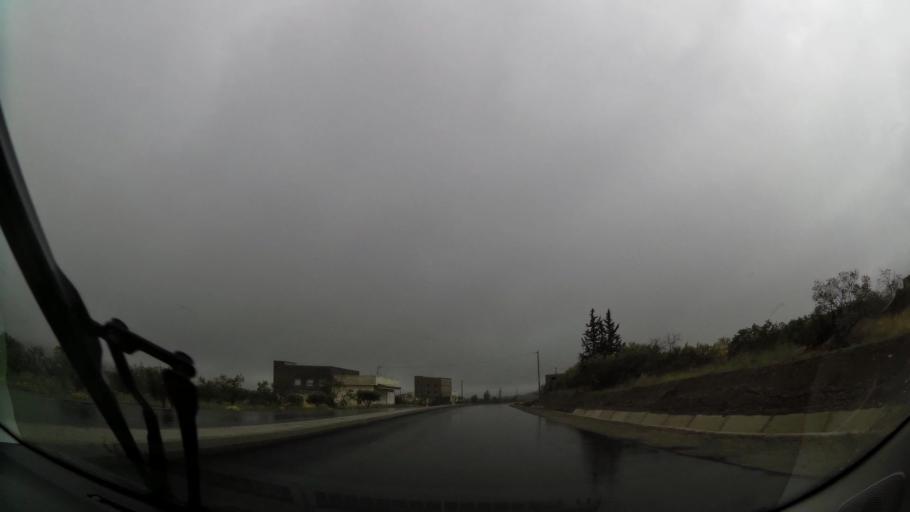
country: MA
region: Oriental
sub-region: Nador
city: Midar
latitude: 34.8600
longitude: -3.7227
